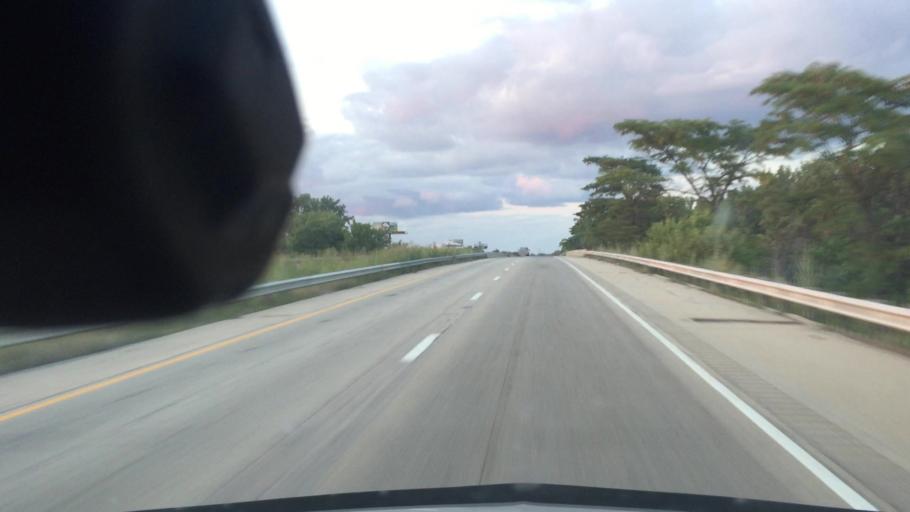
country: US
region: Illinois
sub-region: Grundy County
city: Central City
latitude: 41.2225
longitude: -88.2813
